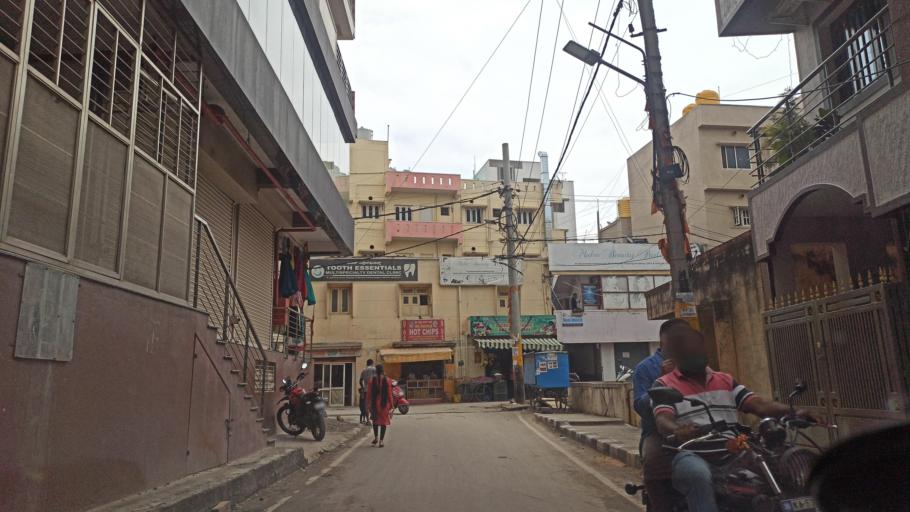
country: IN
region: Karnataka
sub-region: Bangalore Urban
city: Bangalore
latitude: 12.9944
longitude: 77.6728
